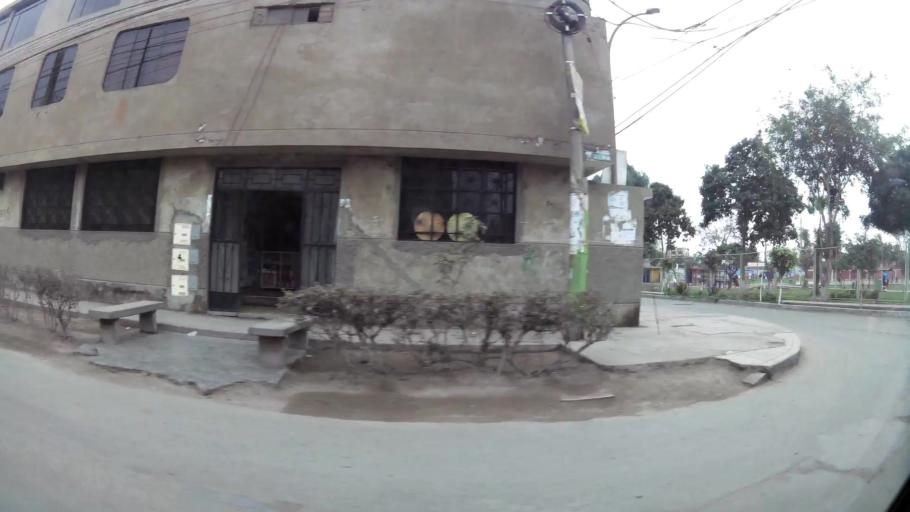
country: PE
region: Lima
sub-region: Lima
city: Independencia
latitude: -11.9671
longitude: -77.0583
